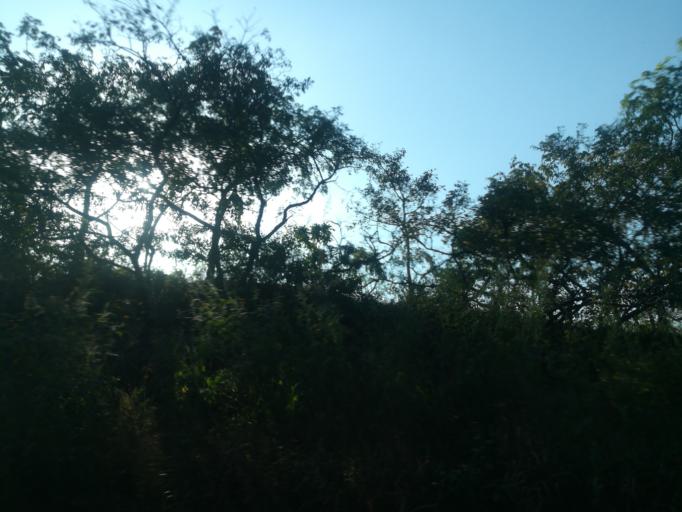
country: NG
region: Ogun
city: Abeokuta
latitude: 7.2343
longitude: 3.3008
